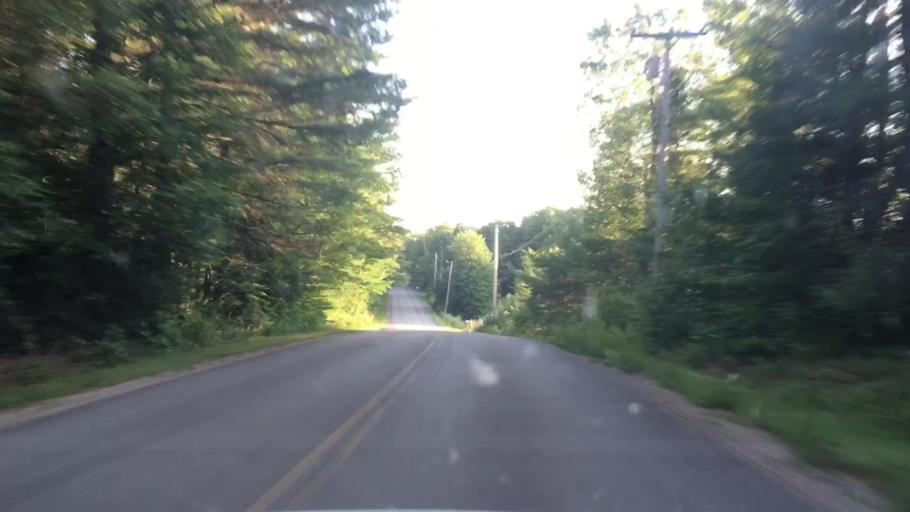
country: US
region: Maine
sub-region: Penobscot County
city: Hampden
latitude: 44.7101
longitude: -68.8876
